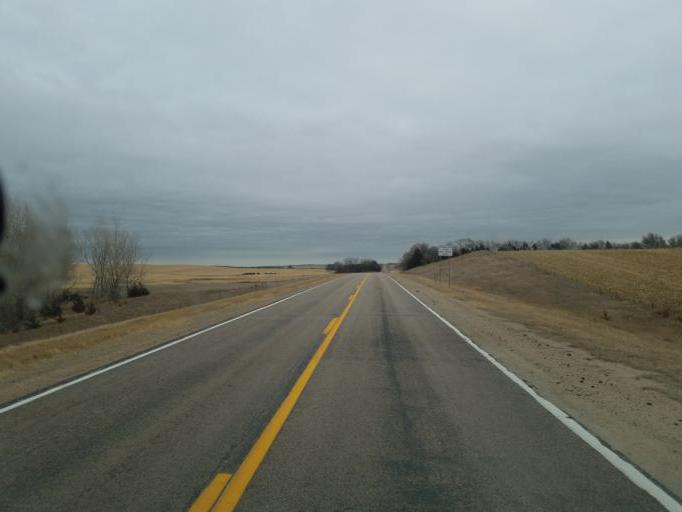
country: US
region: Nebraska
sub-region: Cedar County
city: Hartington
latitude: 42.6128
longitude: -97.4490
